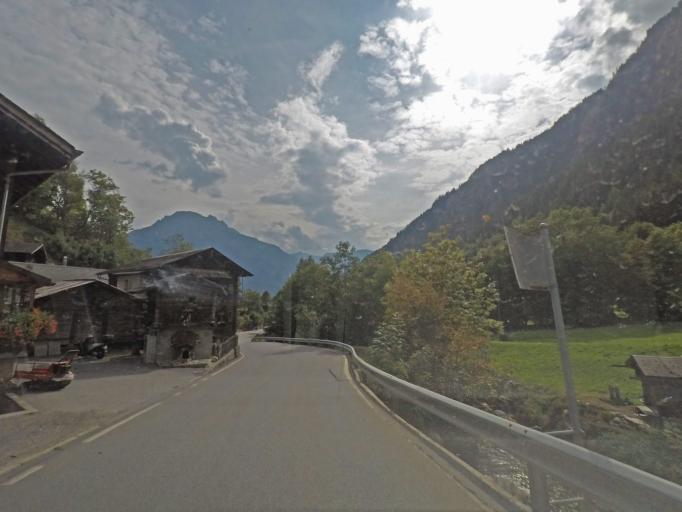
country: CH
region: Valais
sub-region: Brig District
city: Naters
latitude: 46.3428
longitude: 7.9840
